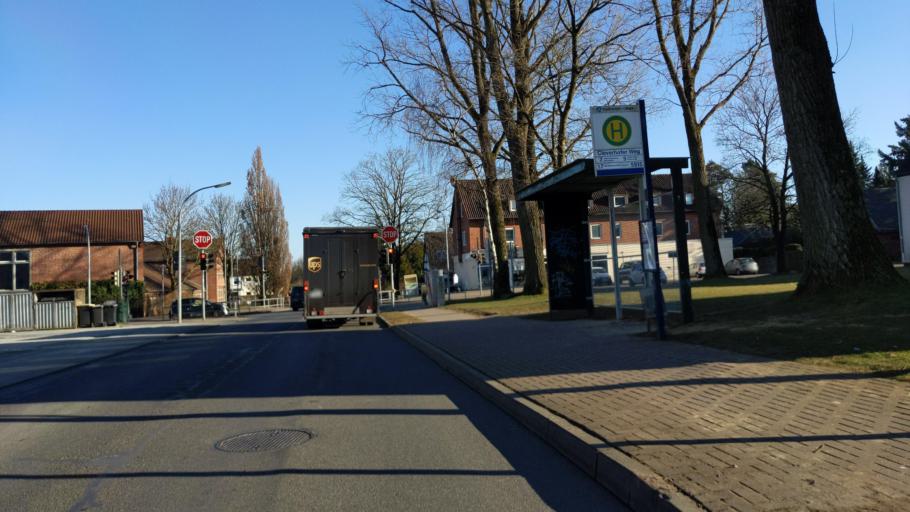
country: DE
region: Schleswig-Holstein
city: Bad Schwartau
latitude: 53.9101
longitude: 10.6776
